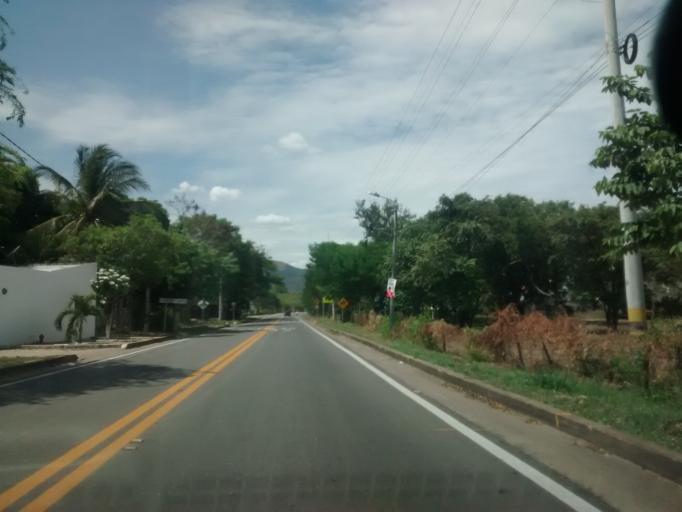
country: CO
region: Cundinamarca
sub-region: Girardot
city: Girardot City
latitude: 4.3440
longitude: -74.8038
